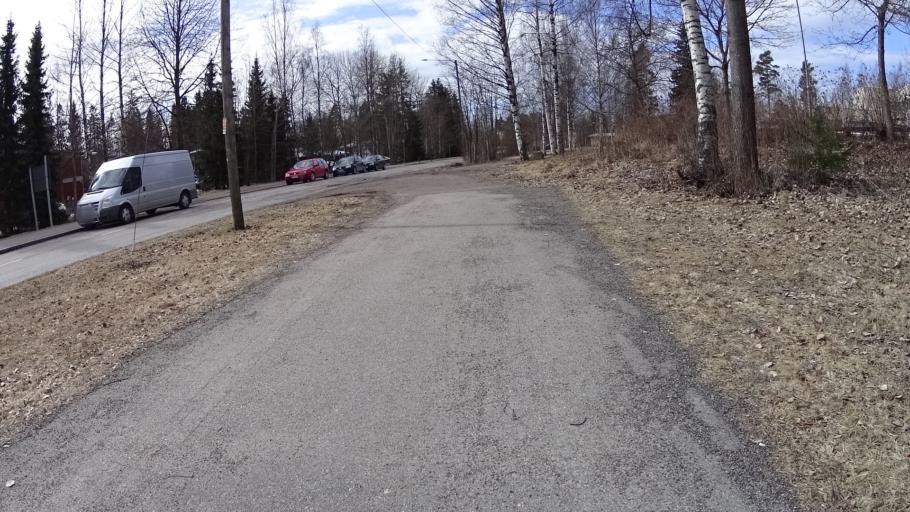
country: FI
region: Uusimaa
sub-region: Helsinki
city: Kilo
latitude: 60.2376
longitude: 24.8209
